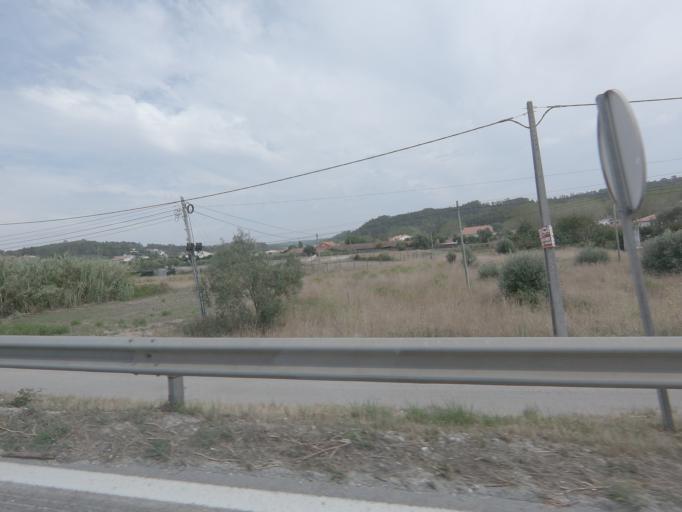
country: PT
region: Leiria
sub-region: Leiria
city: Caranguejeira
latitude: 39.8088
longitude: -8.7416
